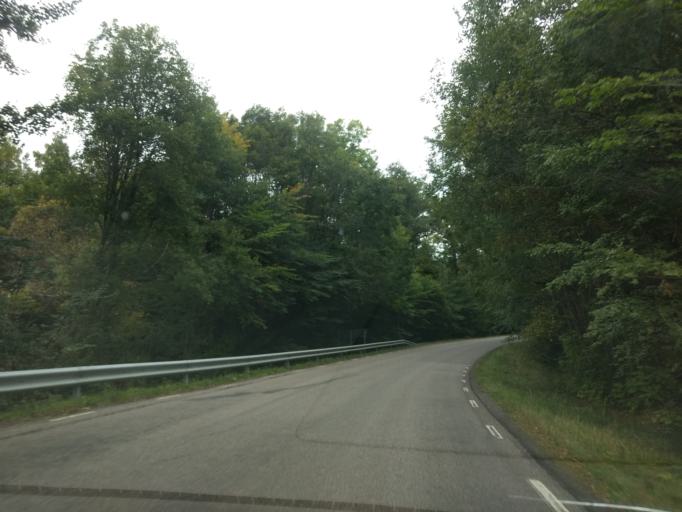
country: SE
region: Uppsala
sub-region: Habo Kommun
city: Balsta
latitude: 59.6789
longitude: 17.5331
